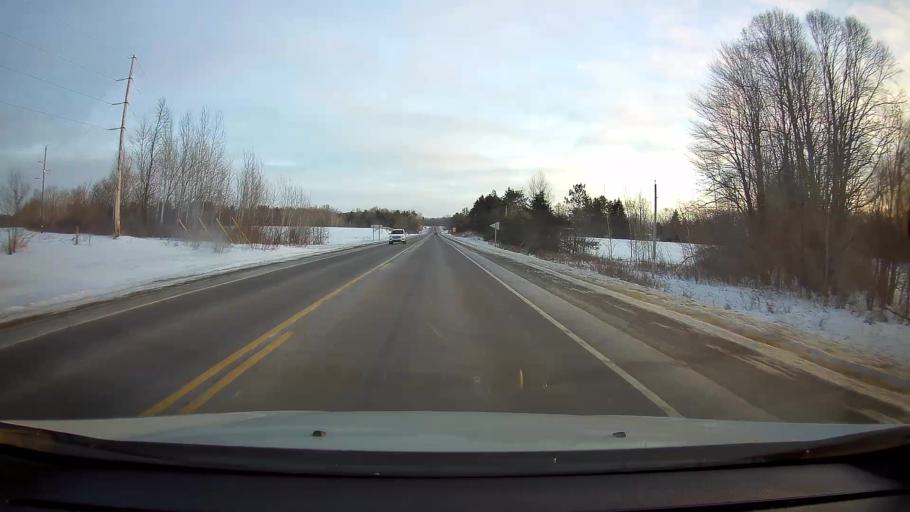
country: US
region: Wisconsin
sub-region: Polk County
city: Clear Lake
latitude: 45.2600
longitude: -92.2605
